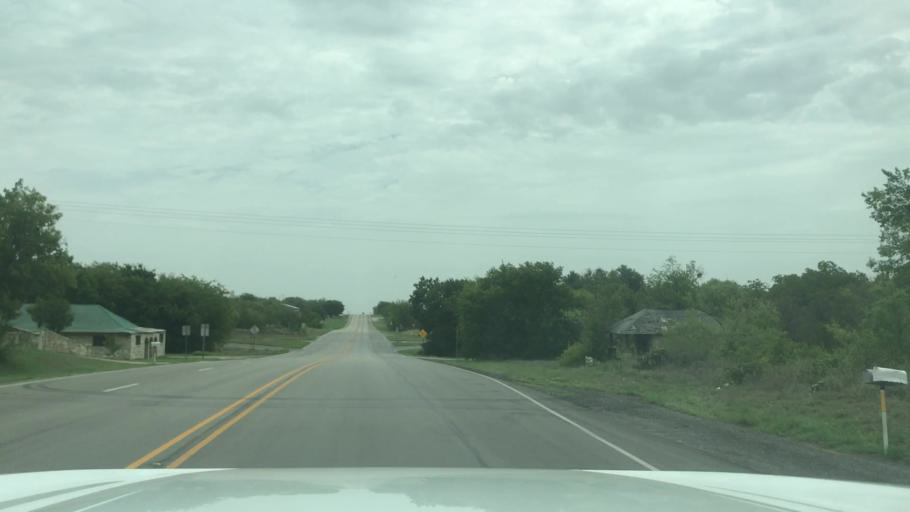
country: US
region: Texas
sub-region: Erath County
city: Dublin
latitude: 32.0592
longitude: -98.2083
